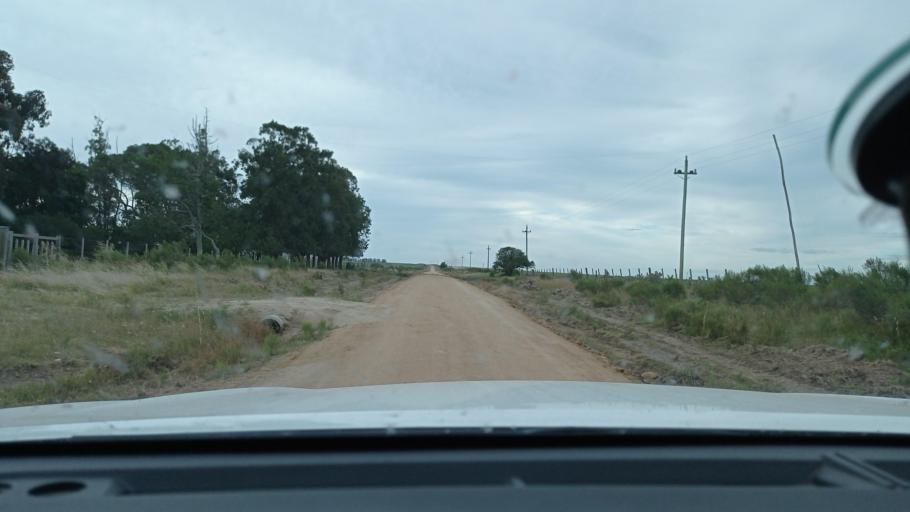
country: UY
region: Florida
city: Casupa
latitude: -34.1081
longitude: -55.7643
